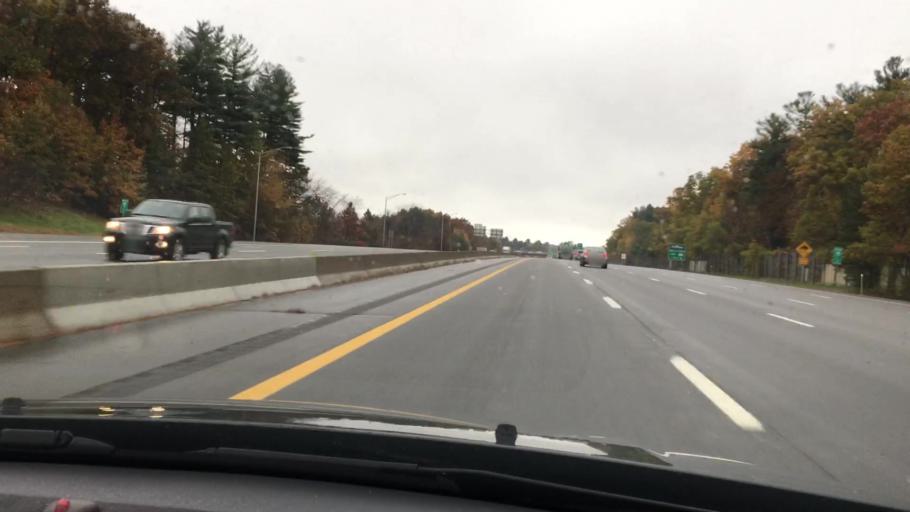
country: US
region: New Hampshire
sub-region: Hillsborough County
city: Nashua
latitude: 42.7858
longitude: -71.4950
